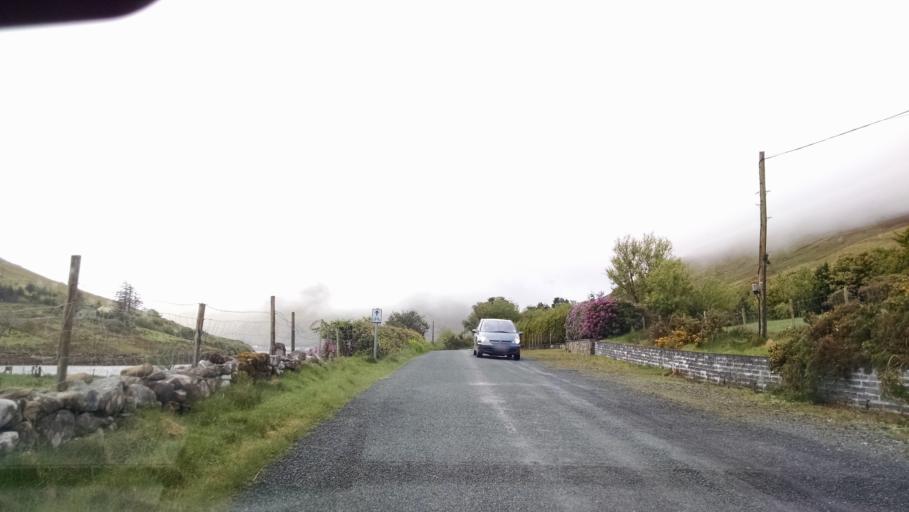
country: IE
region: Connaught
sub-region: Maigh Eo
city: Westport
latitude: 53.6095
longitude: -9.6842
